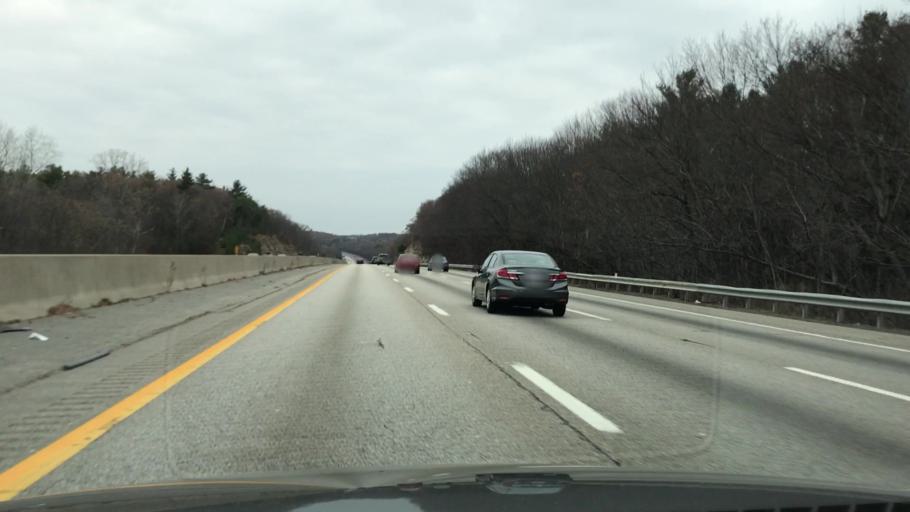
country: US
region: Massachusetts
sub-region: Worcester County
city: Westborough
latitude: 42.2271
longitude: -71.6372
